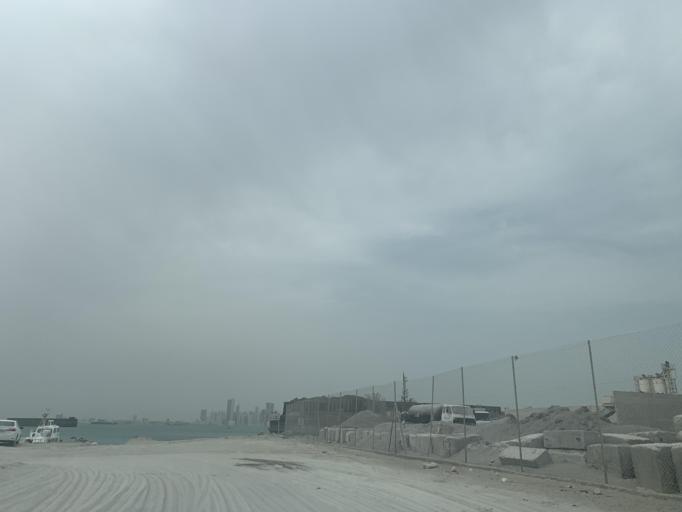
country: BH
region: Muharraq
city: Al Hadd
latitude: 26.2110
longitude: 50.6558
